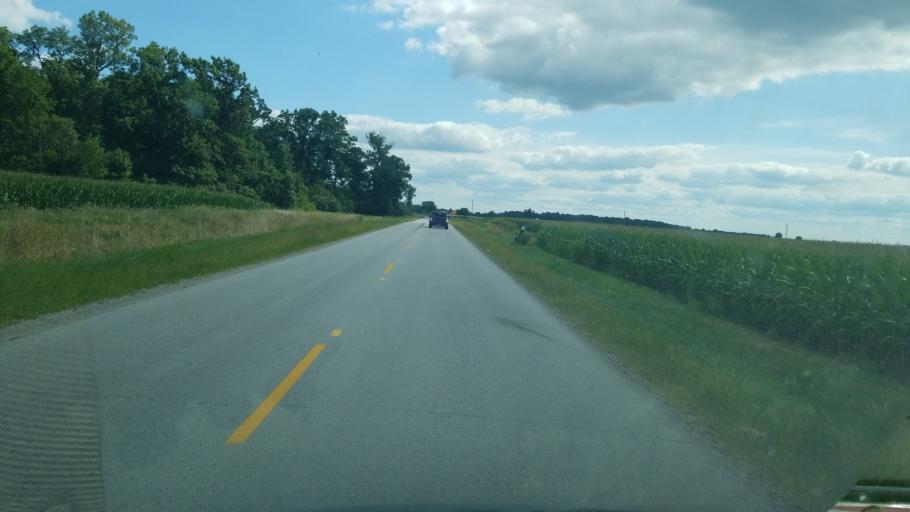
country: US
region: Ohio
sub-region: Logan County
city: Lakeview
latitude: 40.5610
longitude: -83.9755
